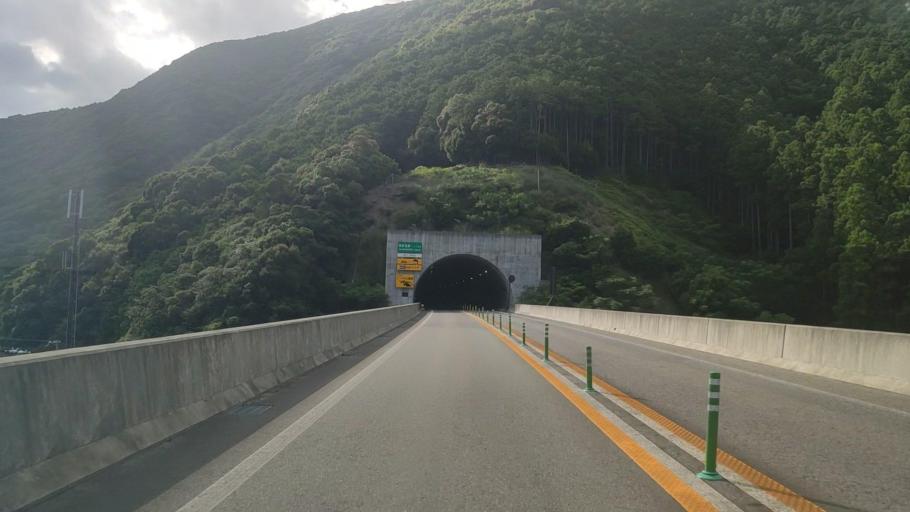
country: JP
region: Wakayama
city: Tanabe
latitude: 33.5612
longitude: 135.5044
